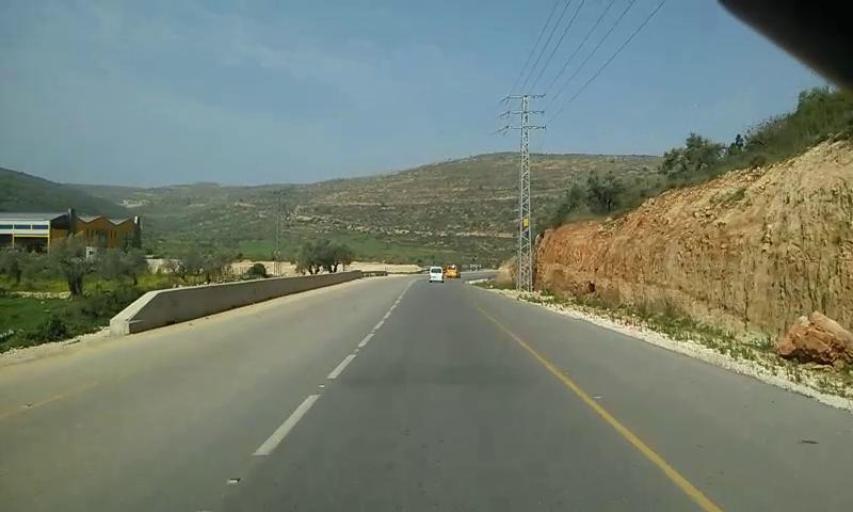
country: PS
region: West Bank
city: Dura al Qar`
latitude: 31.9862
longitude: 35.2287
